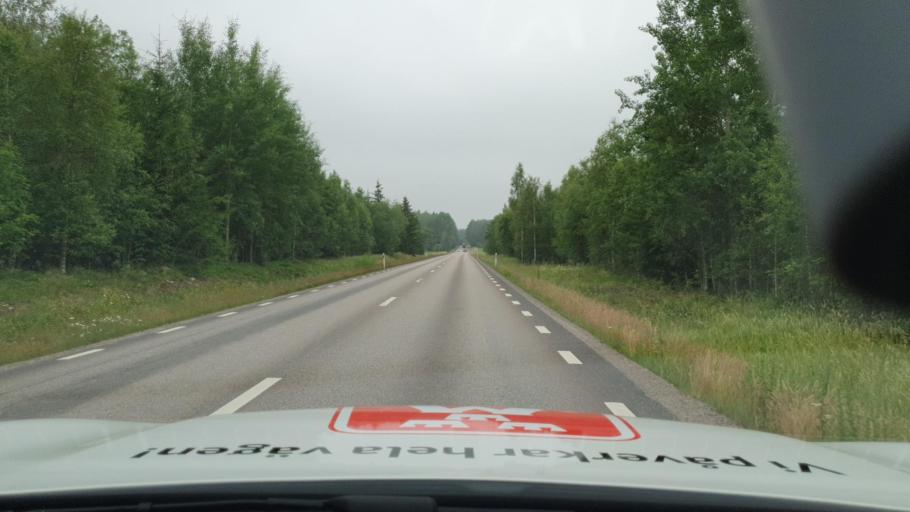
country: SE
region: Vaermland
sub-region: Karlstads Kommun
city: Edsvalla
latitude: 59.6002
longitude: 13.1620
